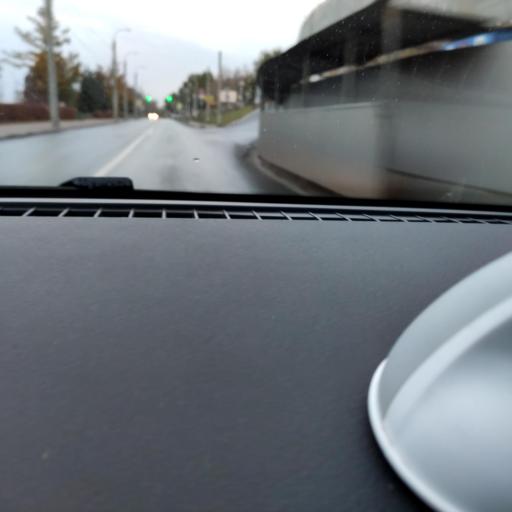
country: RU
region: Samara
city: Rozhdestveno
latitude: 53.1948
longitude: 50.0891
